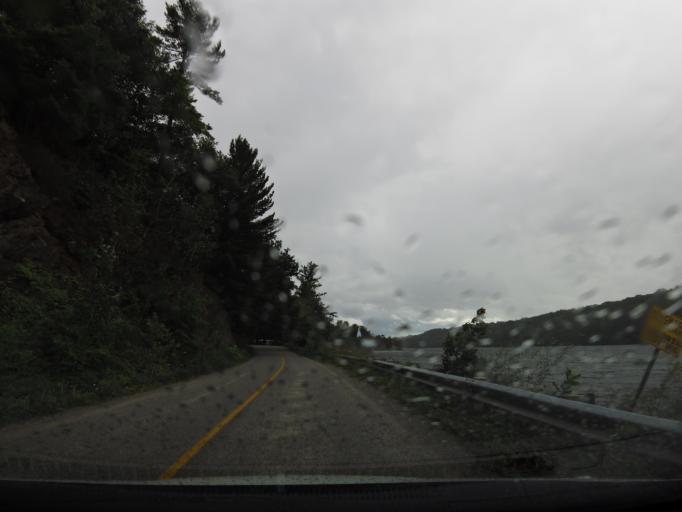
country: CA
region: Ontario
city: Kingston
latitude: 44.6189
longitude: -76.5281
